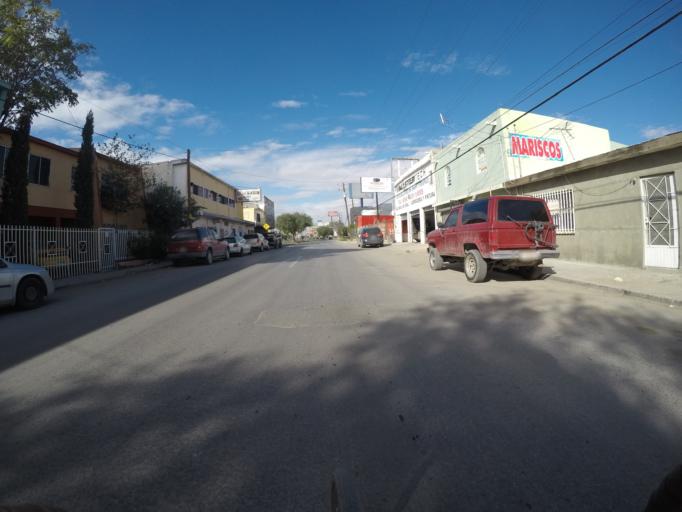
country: MX
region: Chihuahua
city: Ciudad Juarez
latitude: 31.7394
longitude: -106.4268
